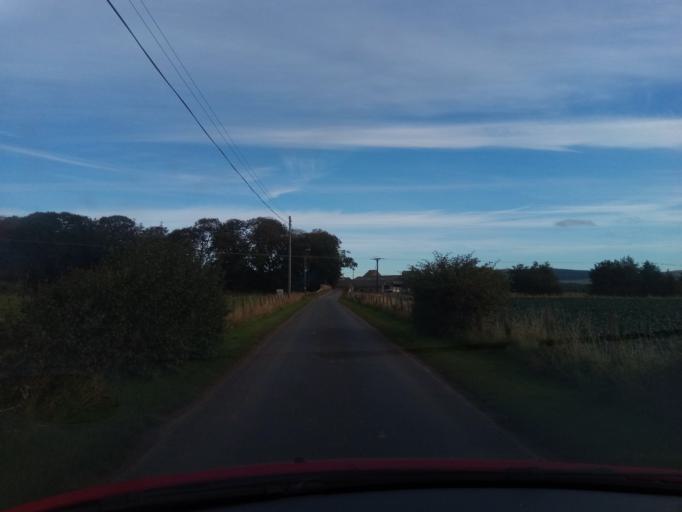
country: GB
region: Scotland
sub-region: The Scottish Borders
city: Kelso
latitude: 55.5232
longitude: -2.4001
